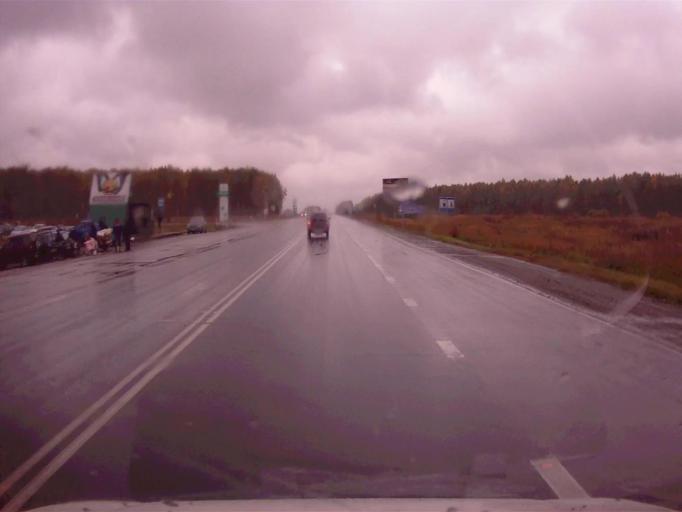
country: RU
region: Chelyabinsk
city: Argayash
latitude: 55.4169
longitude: 61.0264
